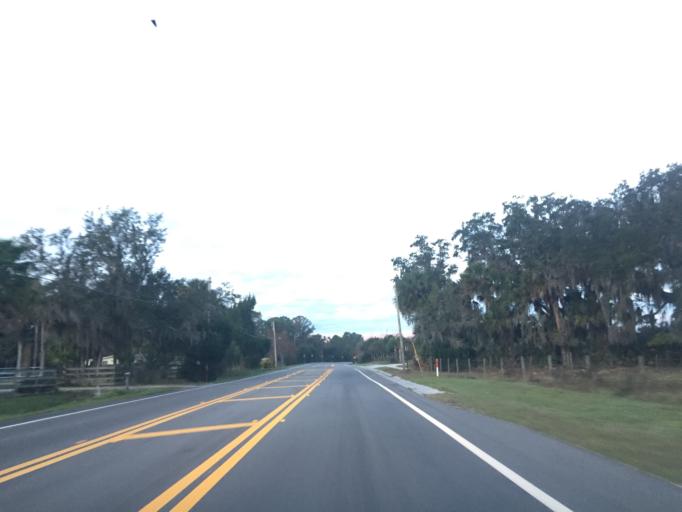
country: US
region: Florida
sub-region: Seminole County
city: Oviedo
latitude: 28.6861
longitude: -81.1626
